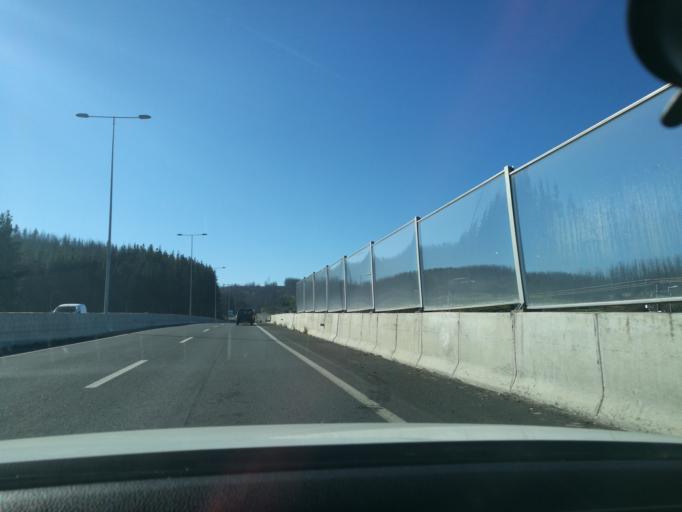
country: CL
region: Biobio
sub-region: Provincia de Concepcion
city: Penco
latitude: -36.8564
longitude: -72.8713
